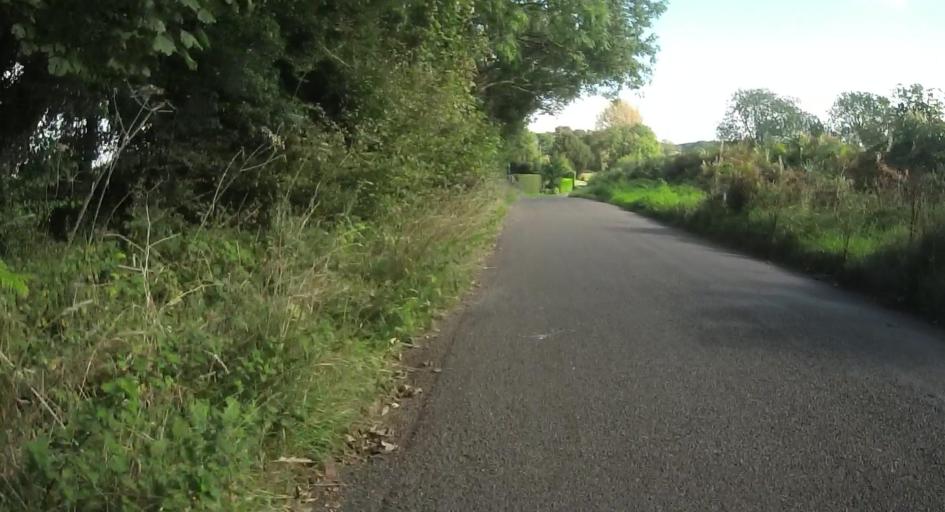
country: GB
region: England
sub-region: Hampshire
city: Four Marks
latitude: 51.1448
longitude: -1.0980
